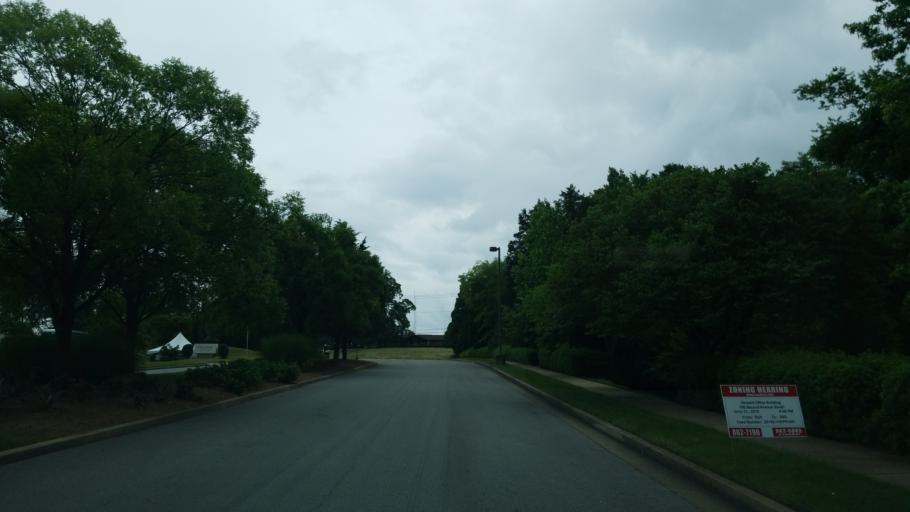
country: US
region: Tennessee
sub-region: Rutherford County
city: La Vergne
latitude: 36.1116
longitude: -86.6415
